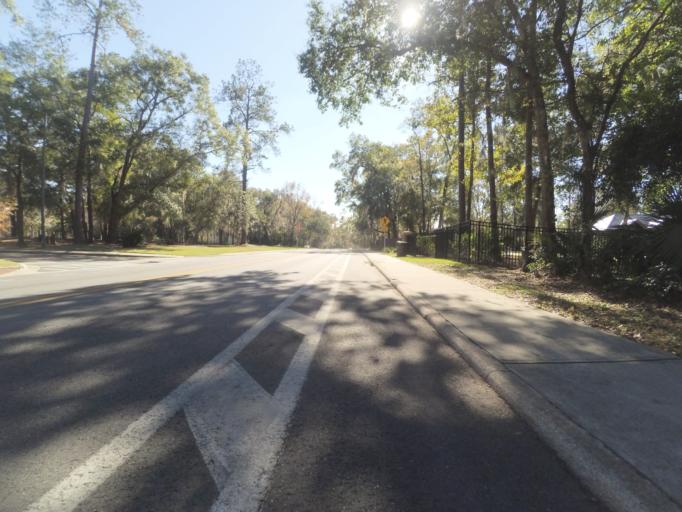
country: US
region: Florida
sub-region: Alachua County
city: Gainesville
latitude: 29.6486
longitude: -82.3603
